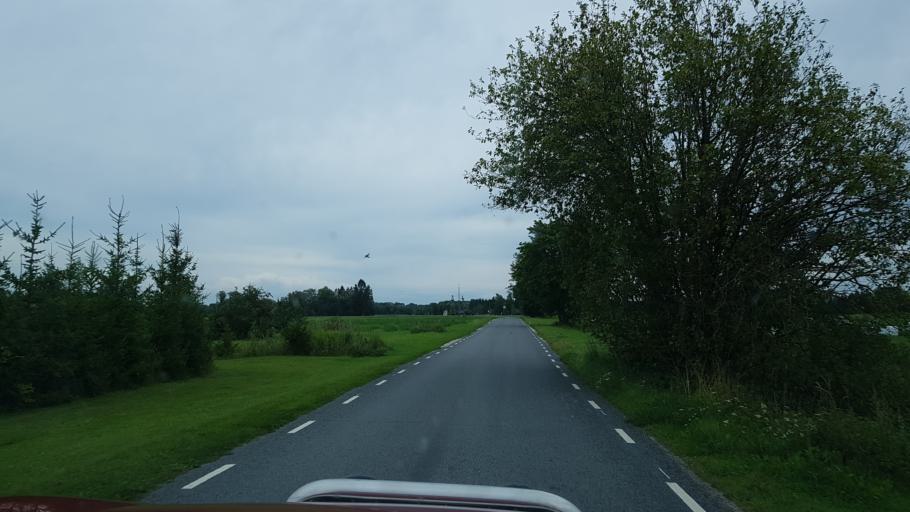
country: EE
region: Harju
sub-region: Nissi vald
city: Turba
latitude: 58.8774
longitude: 24.0806
